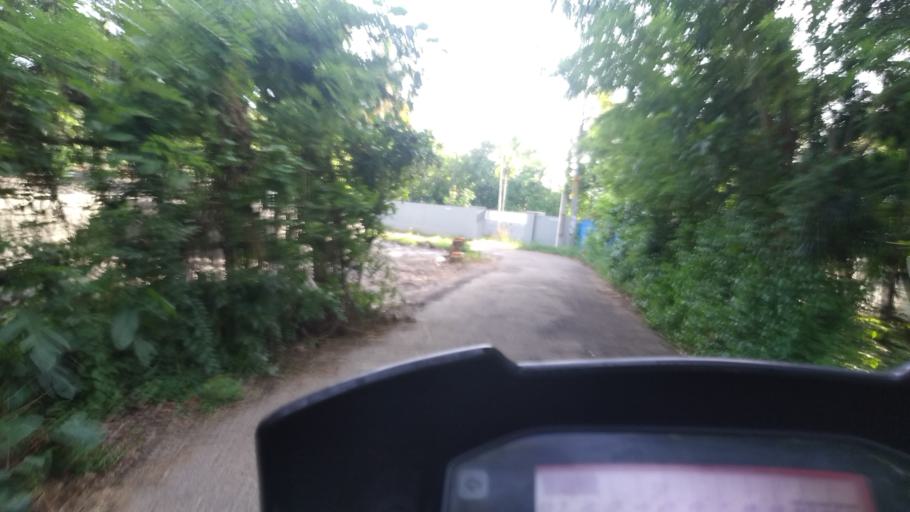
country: IN
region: Kerala
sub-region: Thrissur District
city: Kodungallur
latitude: 10.1332
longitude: 76.1914
